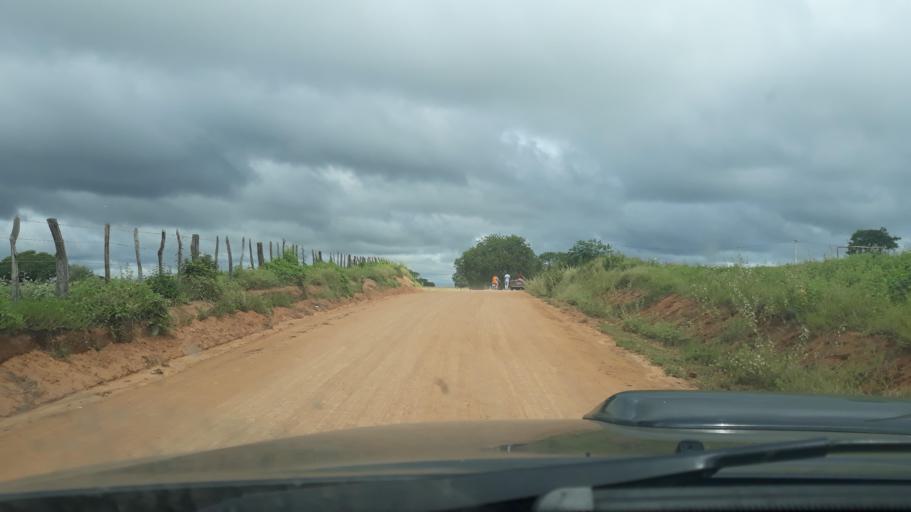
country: BR
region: Bahia
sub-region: Riacho De Santana
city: Riacho de Santana
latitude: -13.9060
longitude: -42.8557
